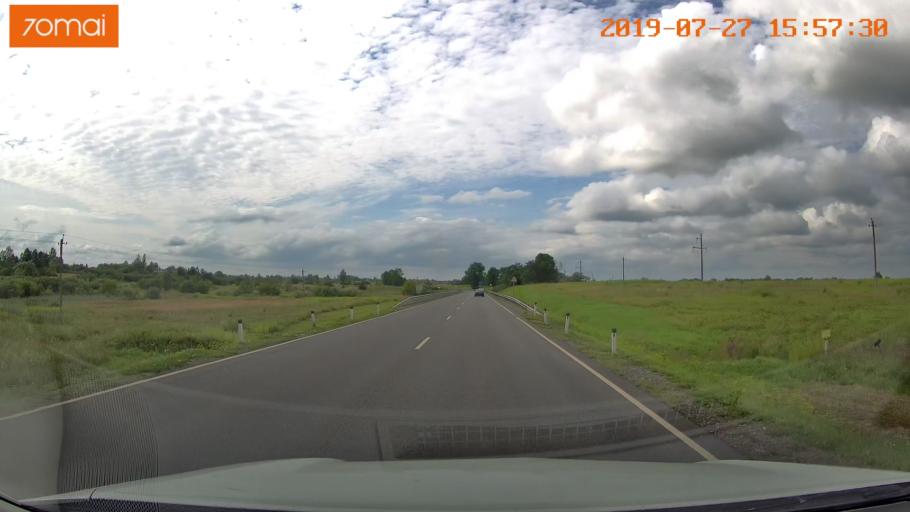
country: RU
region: Kaliningrad
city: Chernyakhovsk
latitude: 54.6237
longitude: 21.8831
